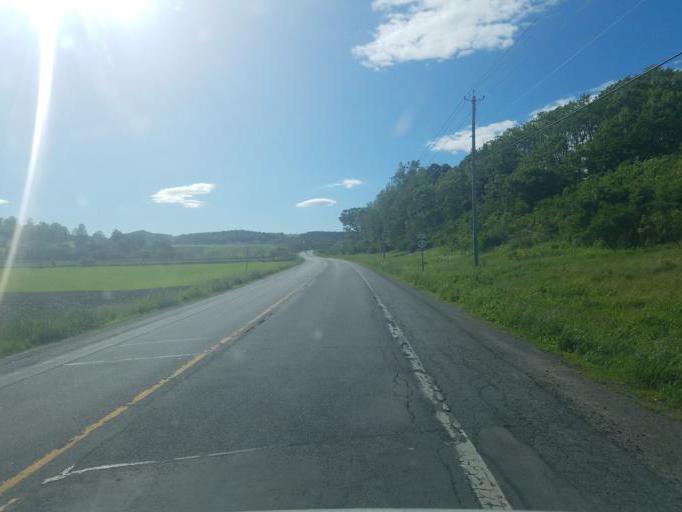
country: US
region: New York
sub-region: Herkimer County
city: Little Falls
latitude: 43.0144
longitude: -74.8049
